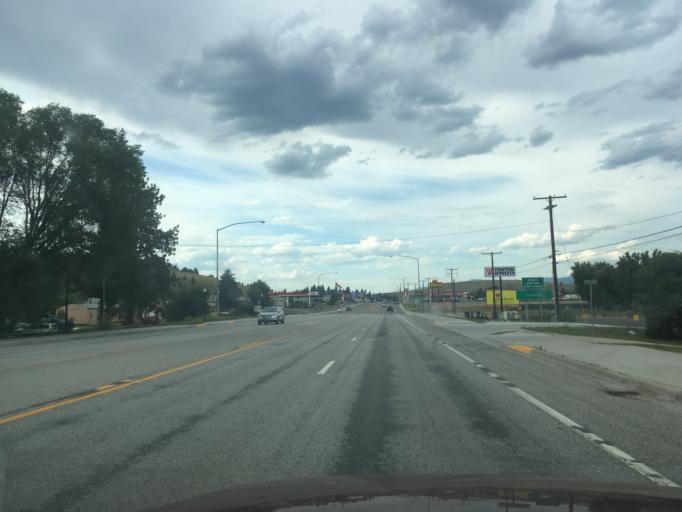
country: US
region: Montana
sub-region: Missoula County
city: Lolo
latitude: 46.7535
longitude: -114.0825
